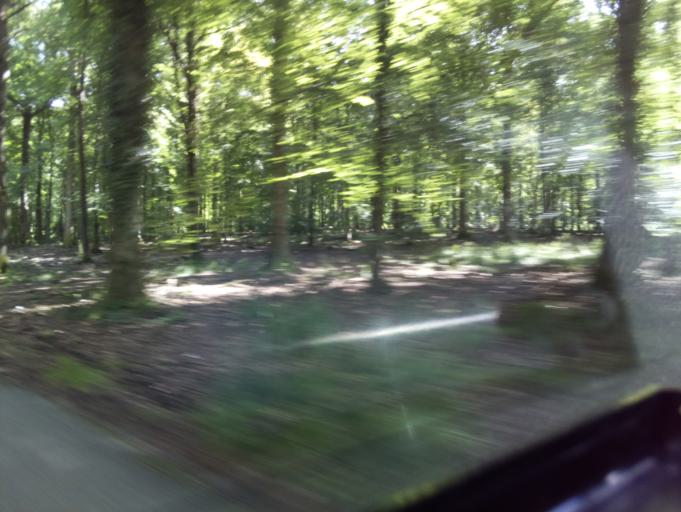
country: GB
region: England
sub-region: Gloucestershire
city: Cinderford
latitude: 51.7829
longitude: -2.4991
